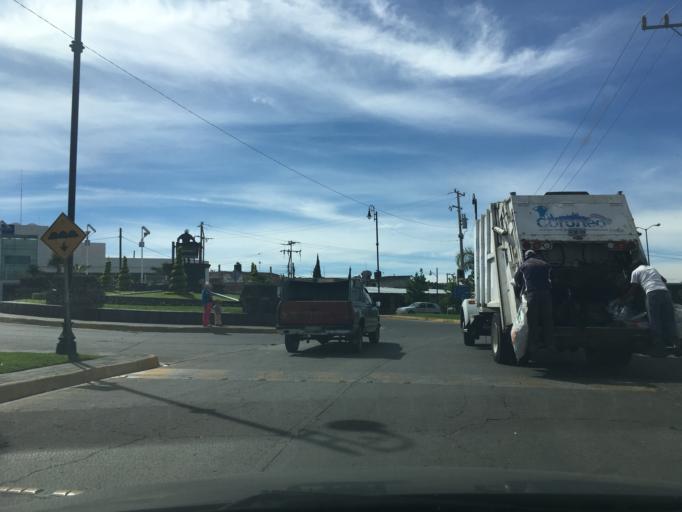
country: MX
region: Guanajuato
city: Coroneo
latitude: 20.1971
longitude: -100.3666
